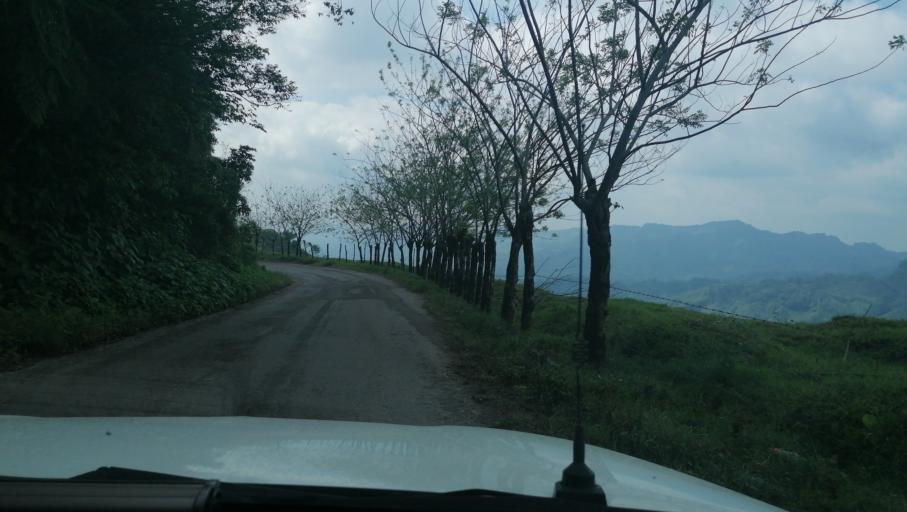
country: MX
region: Chiapas
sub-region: Francisco Leon
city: San Miguel la Sardina
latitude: 17.2389
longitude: -93.3012
